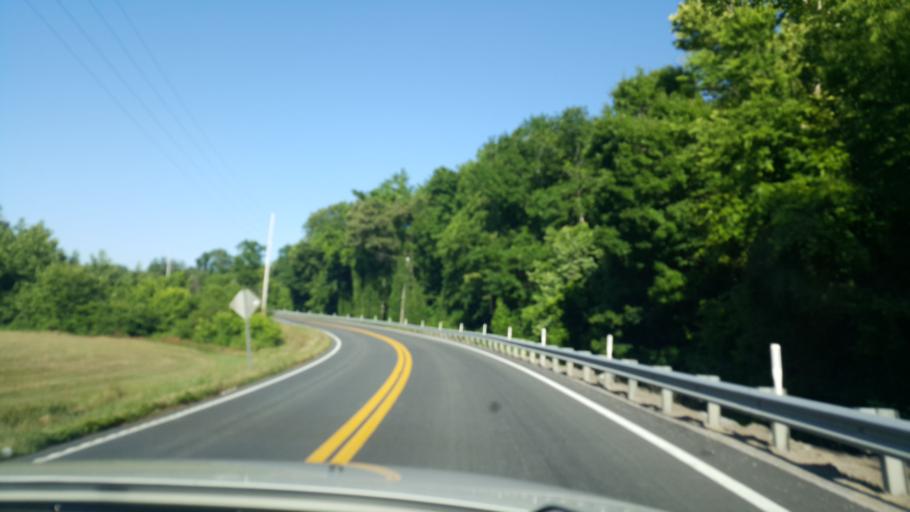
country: US
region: Tennessee
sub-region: Lawrence County
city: Lawrenceburg
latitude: 35.3991
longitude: -87.3852
